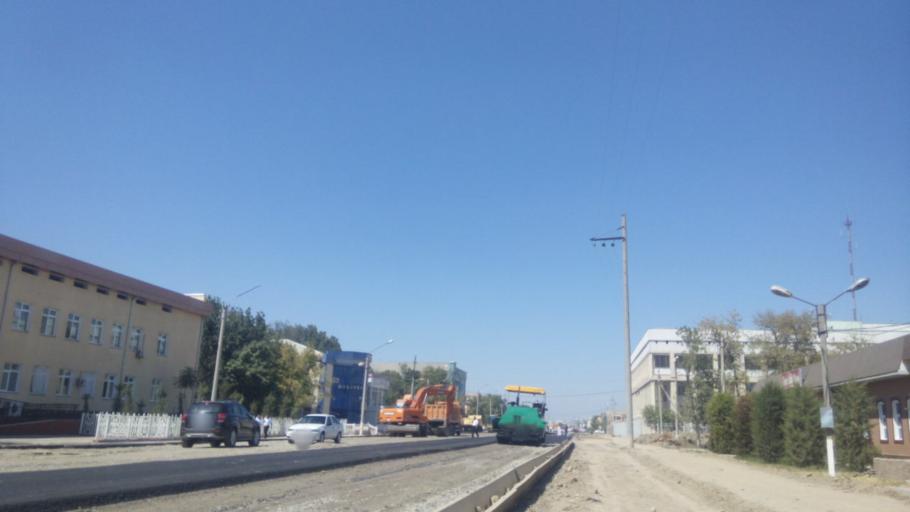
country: UZ
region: Sirdaryo
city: Guliston
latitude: 40.4962
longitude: 68.7737
